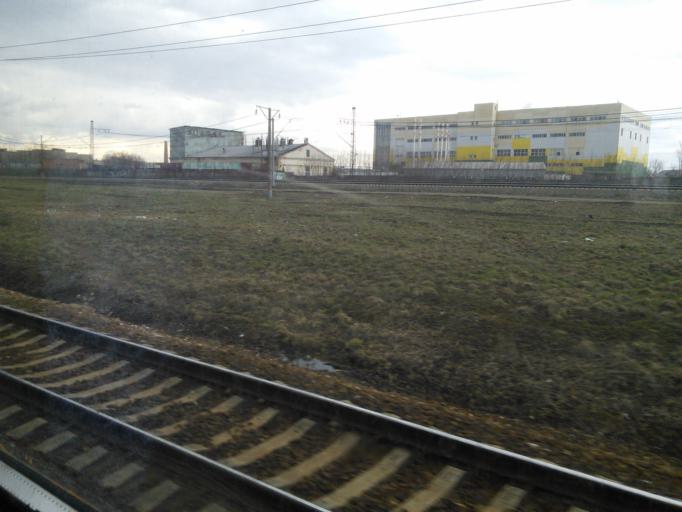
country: RU
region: Moskovskaya
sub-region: Podol'skiy Rayon
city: Podol'sk
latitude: 55.4403
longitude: 37.5681
